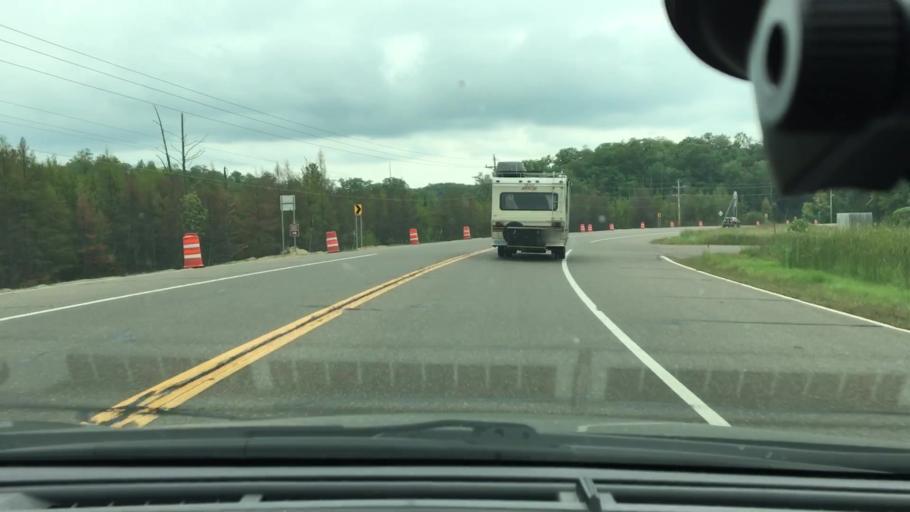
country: US
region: Minnesota
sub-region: Crow Wing County
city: Crosby
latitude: 46.4864
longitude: -93.8996
